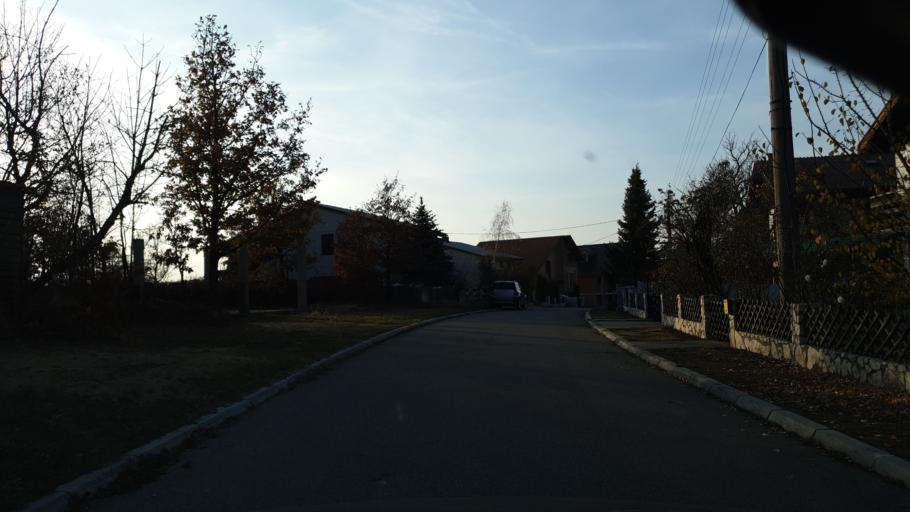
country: RS
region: Central Serbia
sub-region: Borski Okrug
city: Bor
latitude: 44.0553
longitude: 22.0834
